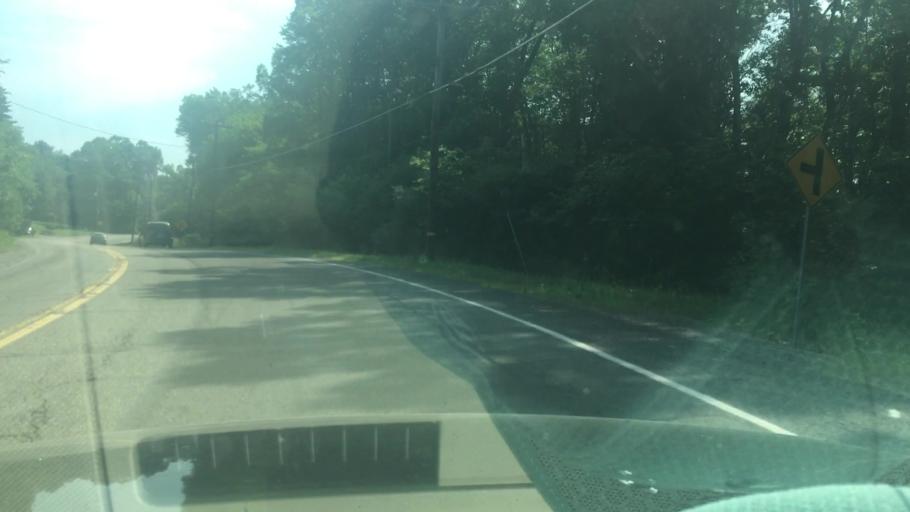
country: US
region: Pennsylvania
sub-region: Schuylkill County
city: Hometown
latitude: 40.8211
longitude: -75.9977
